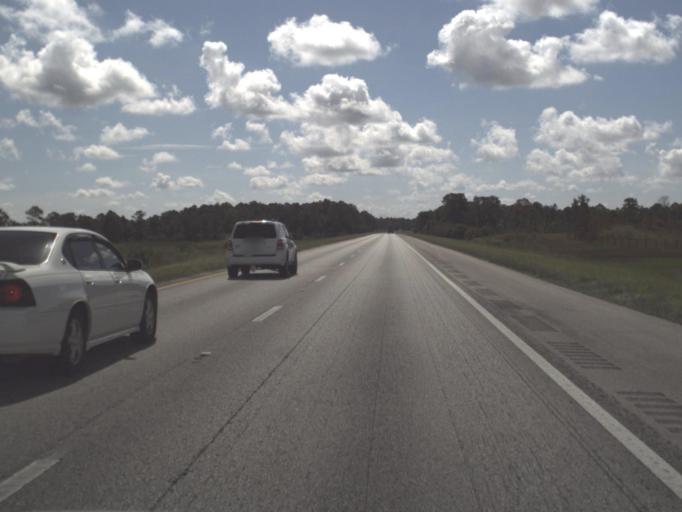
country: US
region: Florida
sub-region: Lee County
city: Suncoast Estates
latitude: 26.8020
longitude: -81.9206
